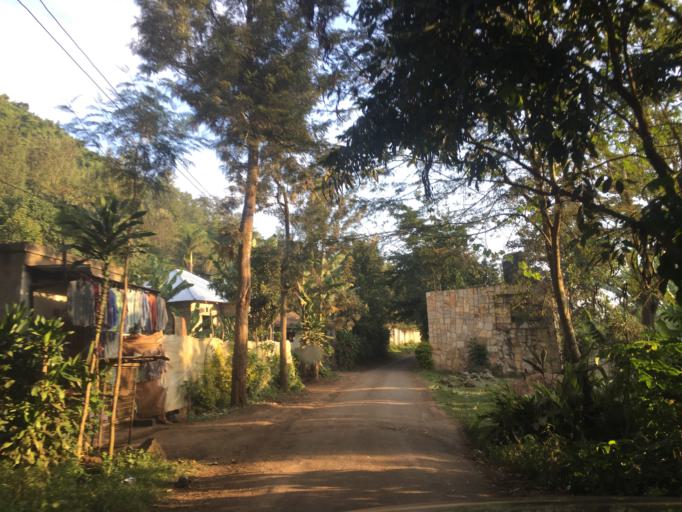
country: TZ
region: Arusha
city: Arusha
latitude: -3.3783
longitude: 36.7460
